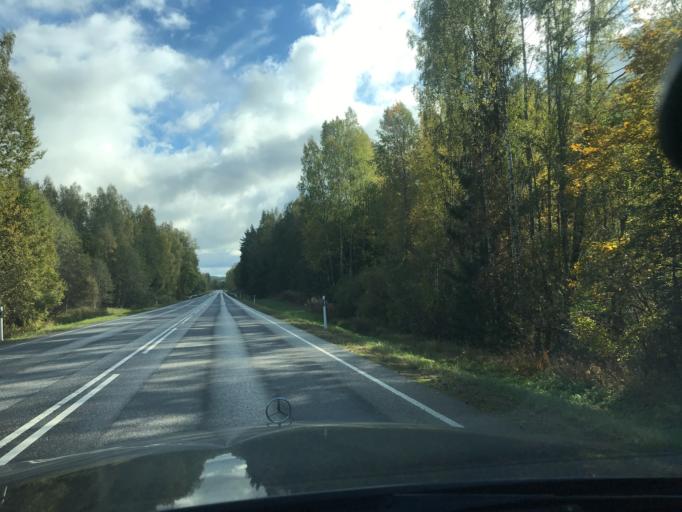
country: EE
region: Vorumaa
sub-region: Voru linn
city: Voru
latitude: 57.7737
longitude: 27.1395
